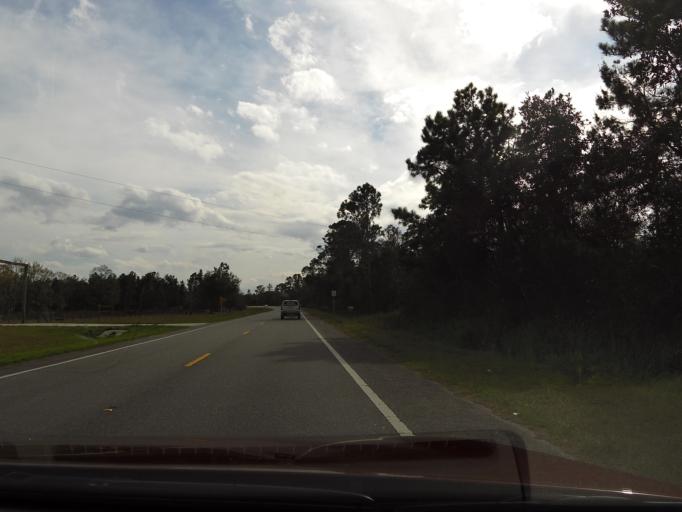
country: US
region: Florida
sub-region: Volusia County
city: De Leon Springs
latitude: 29.1996
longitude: -81.3139
